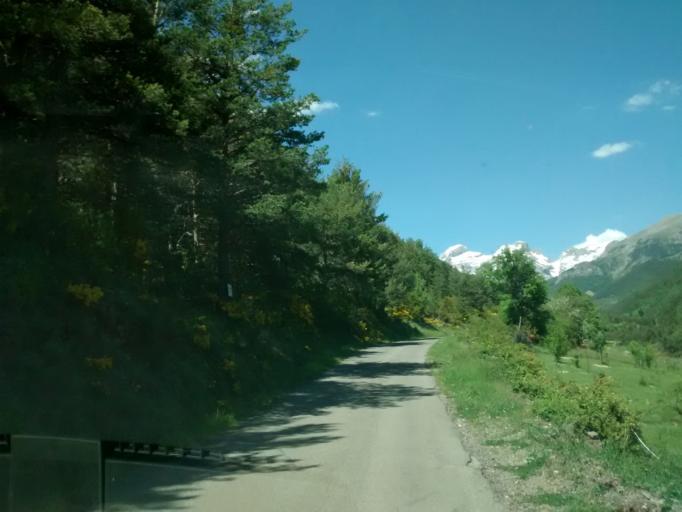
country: ES
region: Aragon
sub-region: Provincia de Huesca
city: Jasa
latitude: 42.6975
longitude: -0.6194
